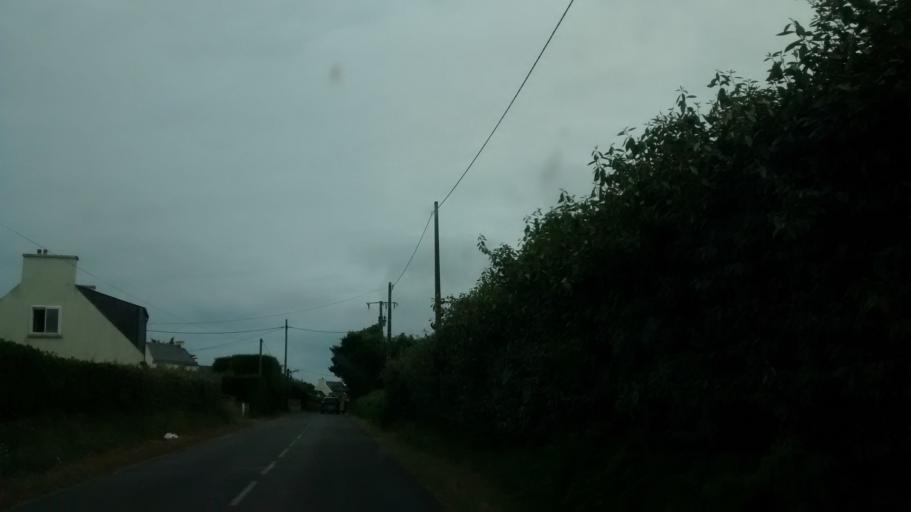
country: FR
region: Brittany
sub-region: Departement du Finistere
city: Guisseny
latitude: 48.6357
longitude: -4.4291
